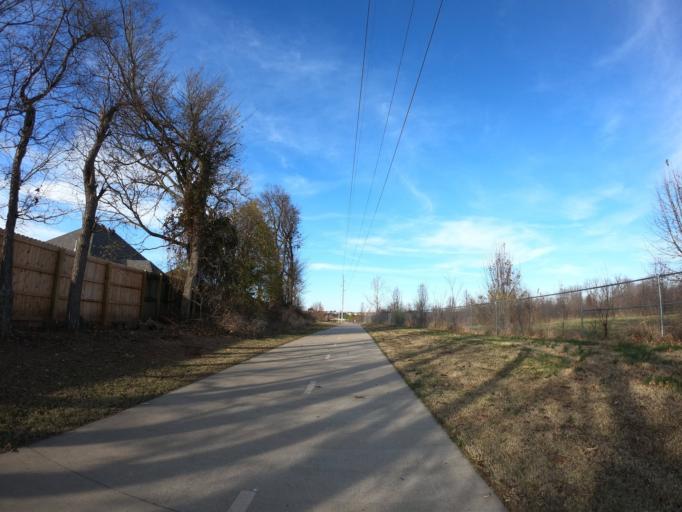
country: US
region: Arkansas
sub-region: Benton County
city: Lowell
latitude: 36.2897
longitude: -94.1654
